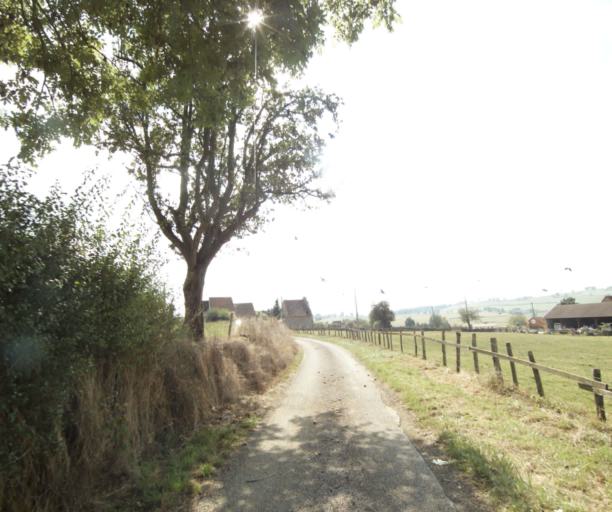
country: FR
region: Bourgogne
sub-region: Departement de Saone-et-Loire
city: Charolles
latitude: 46.3678
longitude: 4.2464
